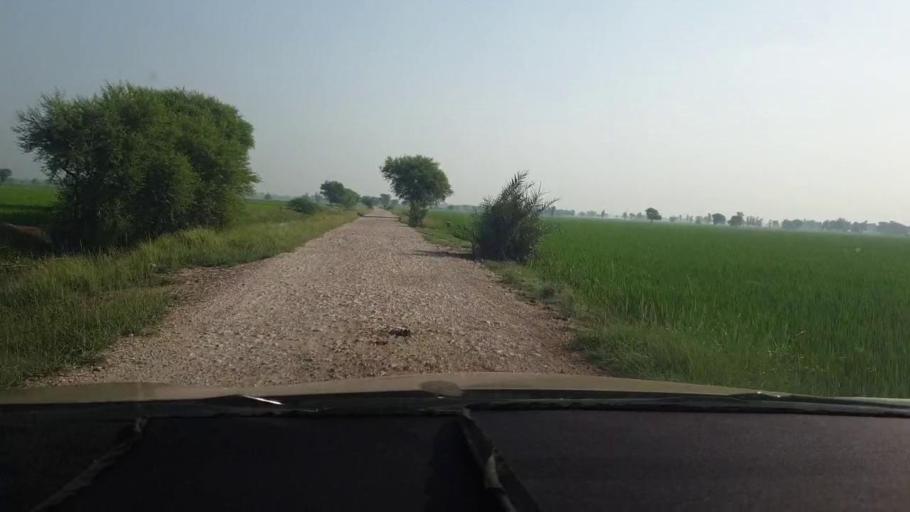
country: PK
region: Sindh
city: Kambar
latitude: 27.5878
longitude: 68.1033
